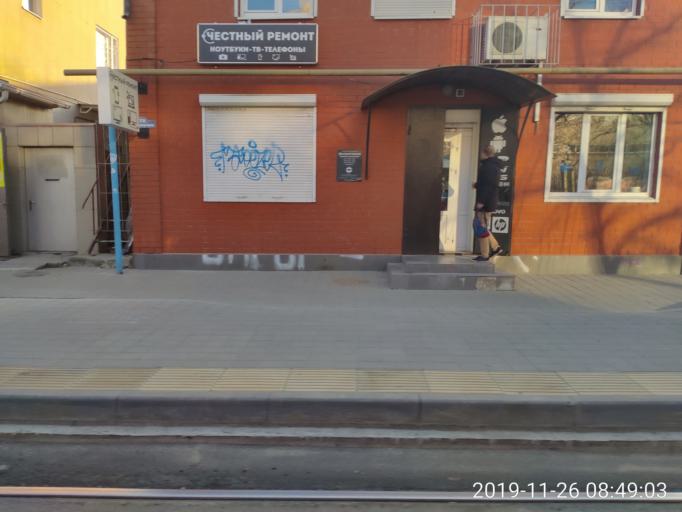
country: RU
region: Krasnodarskiy
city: Krasnodar
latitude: 45.0350
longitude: 38.9783
